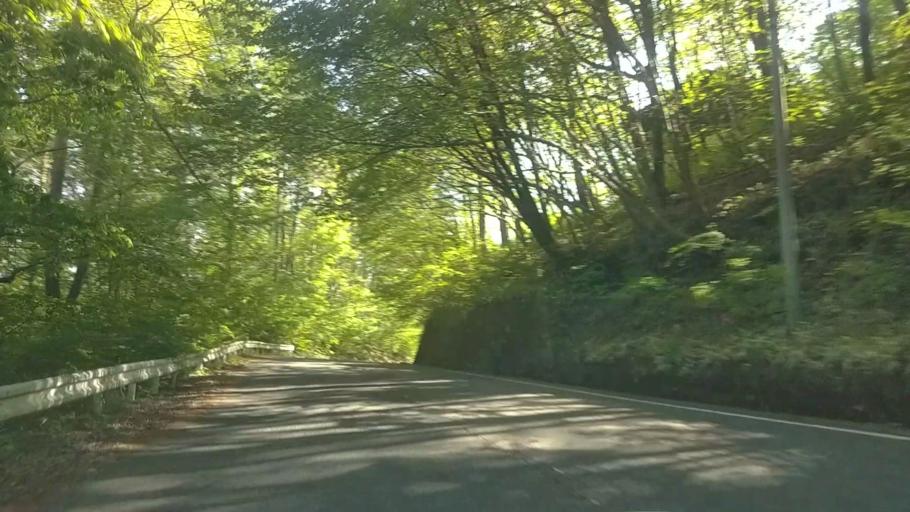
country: JP
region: Yamanashi
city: Nirasaki
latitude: 35.8928
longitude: 138.3990
